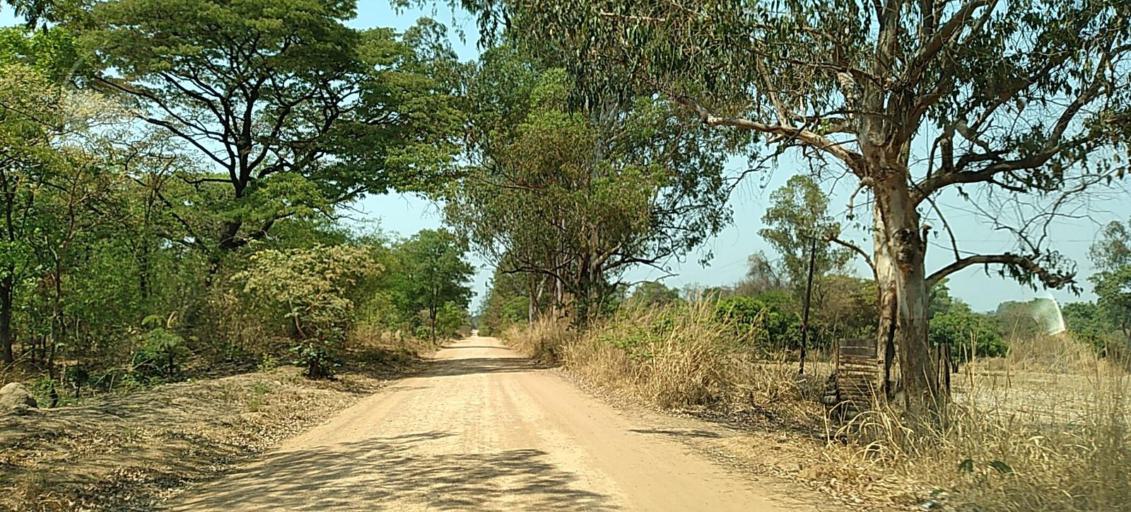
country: ZM
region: Copperbelt
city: Chambishi
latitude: -12.6088
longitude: 27.9591
